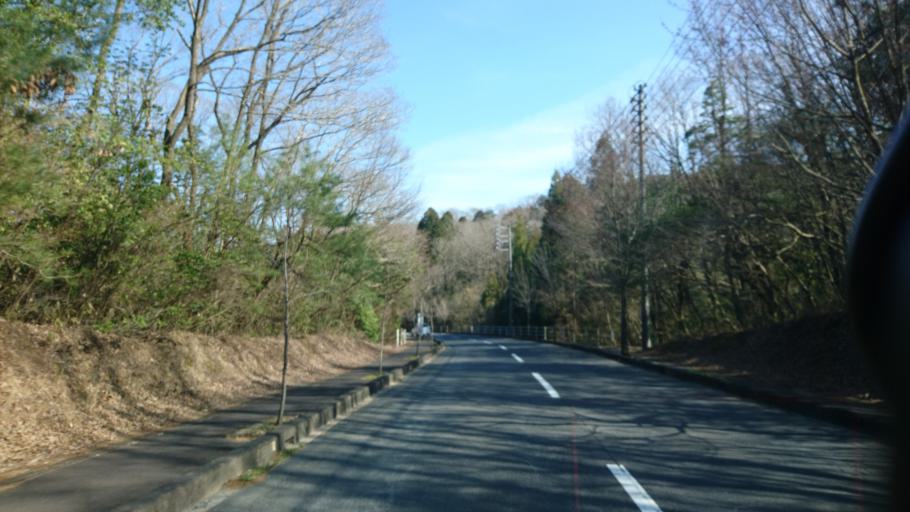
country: JP
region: Gifu
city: Nakatsugawa
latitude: 35.4630
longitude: 137.3931
